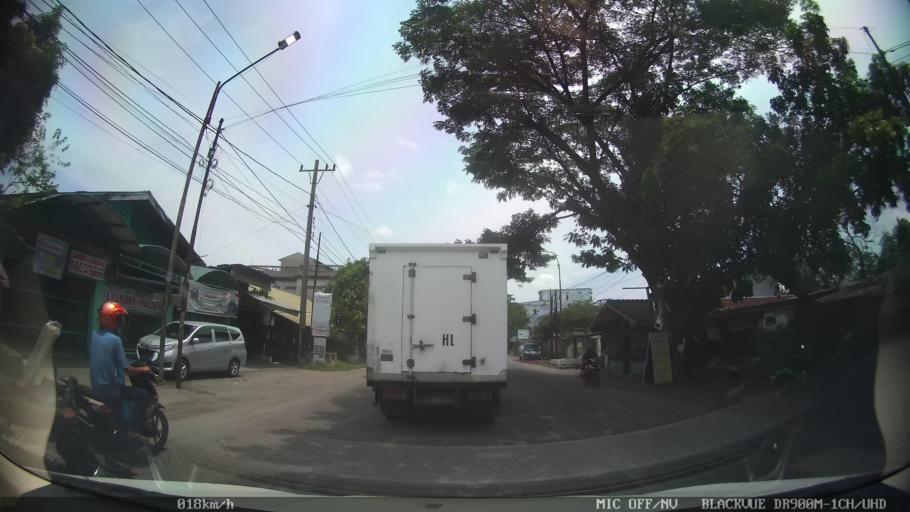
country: ID
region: North Sumatra
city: Labuhan Deli
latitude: 3.7220
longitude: 98.6736
